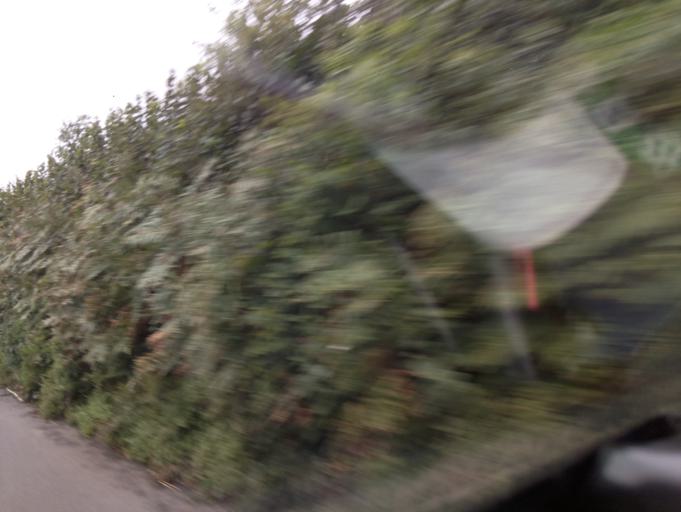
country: GB
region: England
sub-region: Devon
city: Kingsbridge
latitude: 50.2953
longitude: -3.7898
